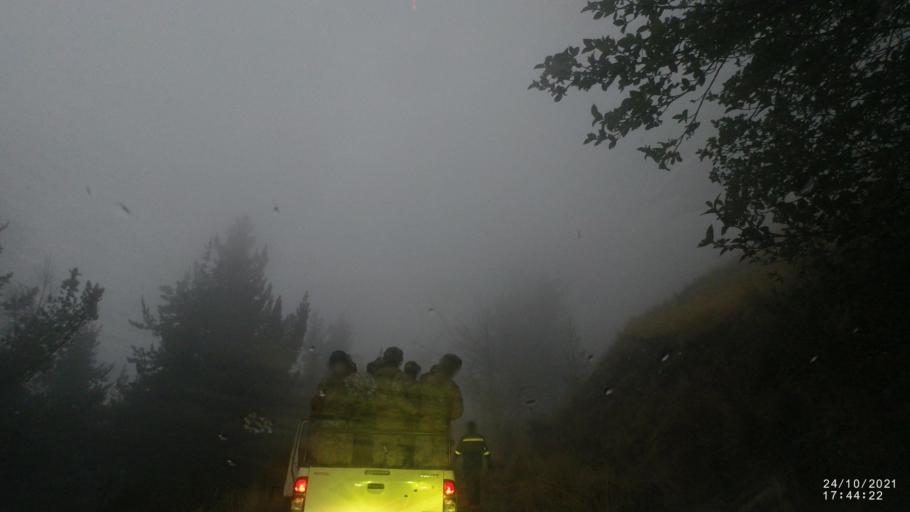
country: BO
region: Cochabamba
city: Cochabamba
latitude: -17.3151
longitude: -66.1346
